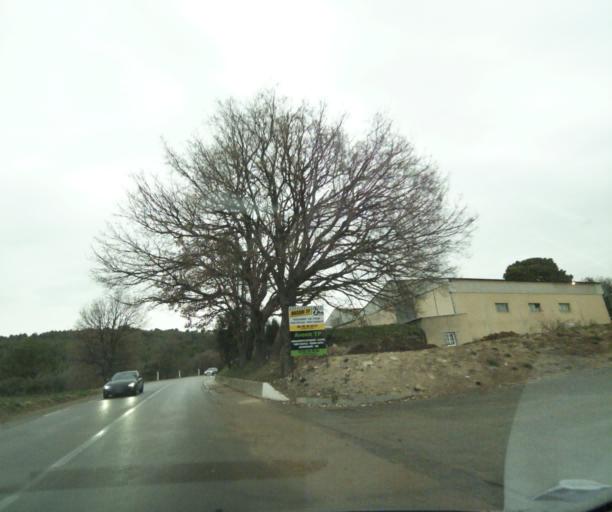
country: FR
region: Provence-Alpes-Cote d'Azur
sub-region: Departement des Bouches-du-Rhone
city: Rognes
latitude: 43.6597
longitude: 5.3641
